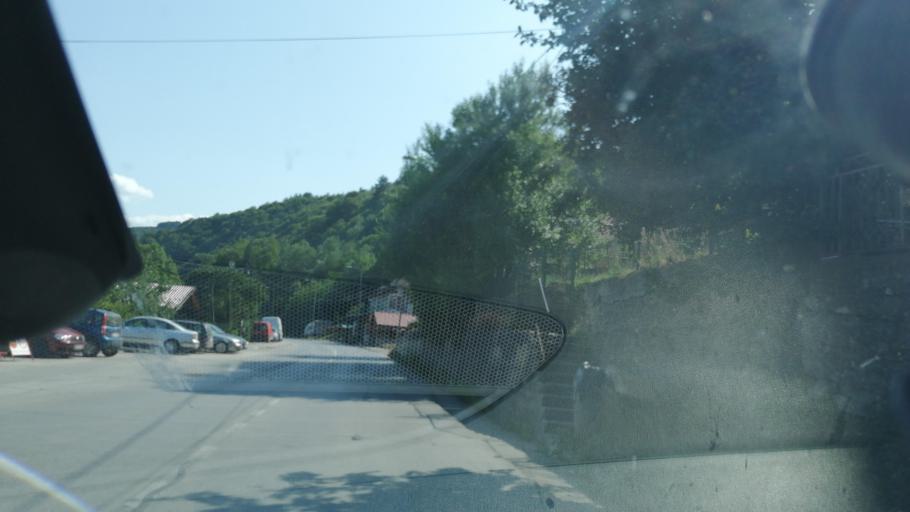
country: RS
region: Central Serbia
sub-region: Moravicki Okrug
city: Ivanjica
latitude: 43.5885
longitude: 20.2239
